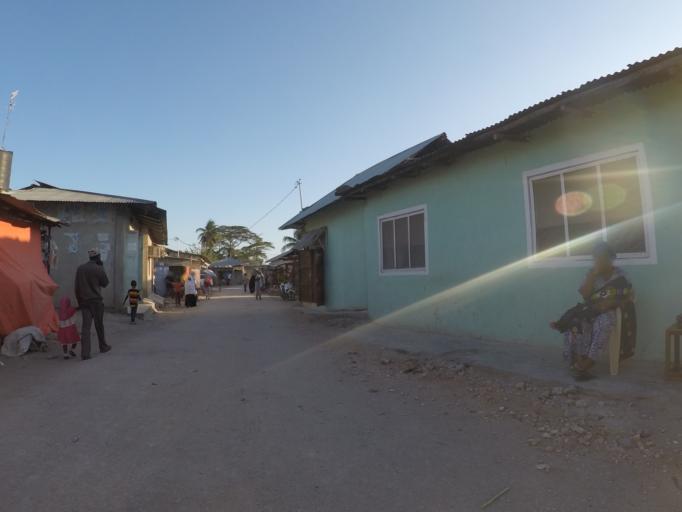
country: TZ
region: Zanzibar Urban/West
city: Zanzibar
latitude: -6.1622
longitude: 39.2176
